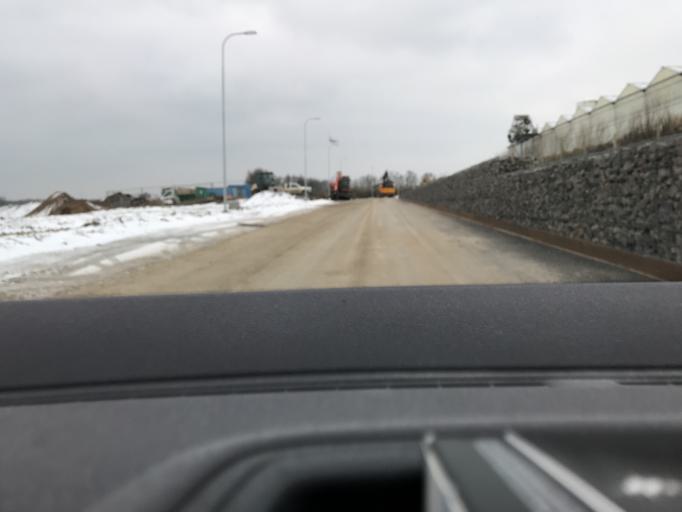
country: SE
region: Skane
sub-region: Ystads Kommun
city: Ystad
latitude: 55.4513
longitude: 13.8544
